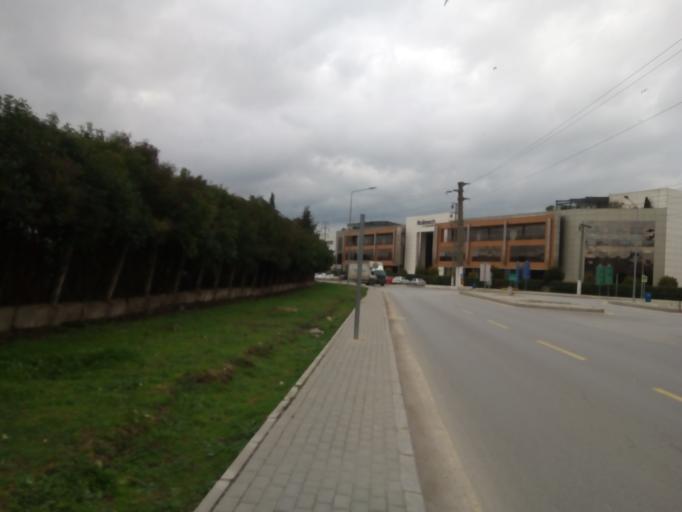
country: TR
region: Bursa
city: Niluefer
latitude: 40.2481
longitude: 28.9558
